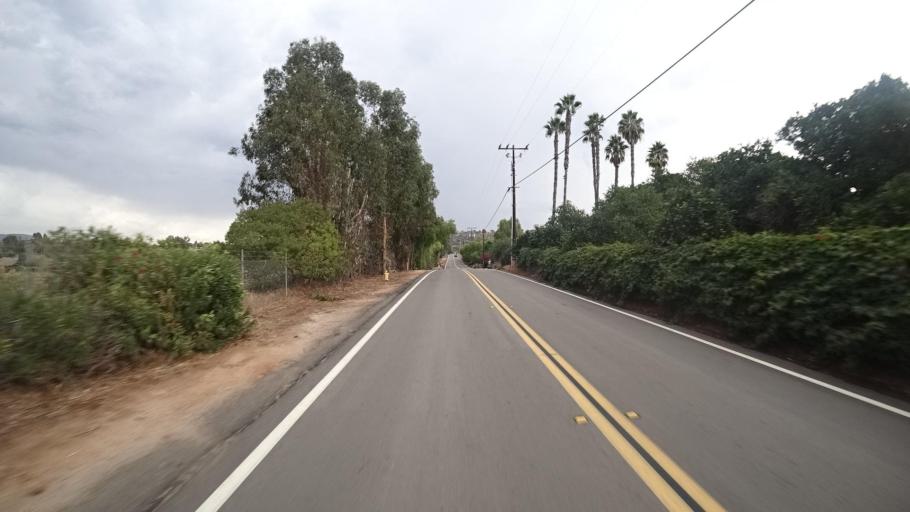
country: US
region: California
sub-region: San Diego County
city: San Pasqual
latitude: 33.0663
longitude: -117.0078
